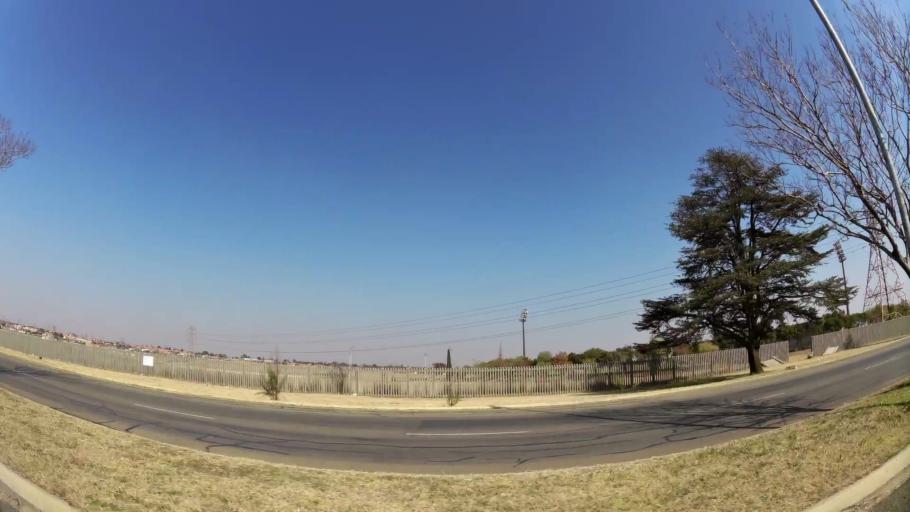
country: ZA
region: Gauteng
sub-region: Ekurhuleni Metropolitan Municipality
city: Boksburg
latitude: -26.2349
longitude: 28.2795
